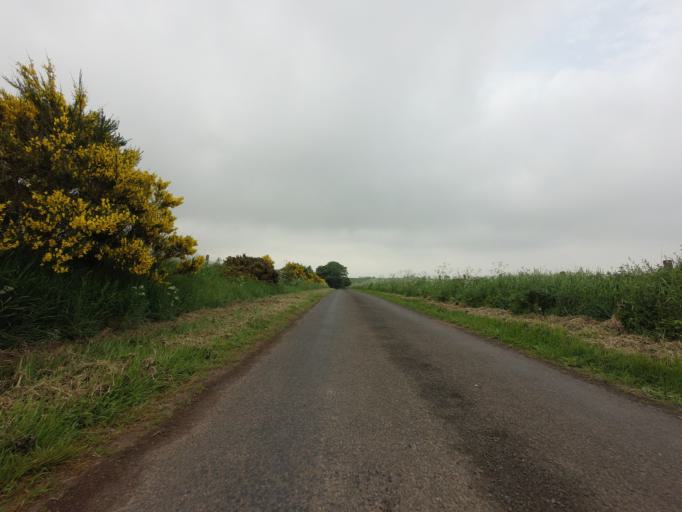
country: GB
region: Scotland
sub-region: Perth and Kinross
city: Milnathort
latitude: 56.2401
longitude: -3.3446
